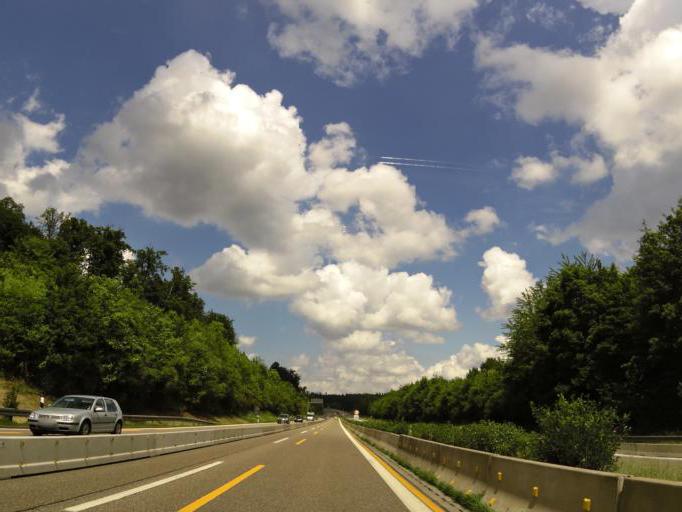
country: DE
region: Baden-Wuerttemberg
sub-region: Regierungsbezirk Stuttgart
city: Nattheim
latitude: 48.6918
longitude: 10.2152
